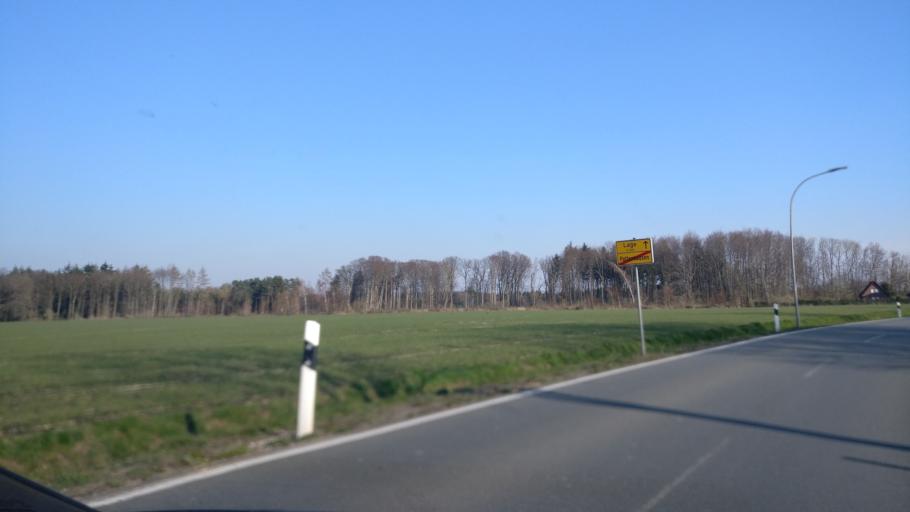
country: DE
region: North Rhine-Westphalia
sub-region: Regierungsbezirk Detmold
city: Leopoldshohe
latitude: 52.0095
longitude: 8.7444
